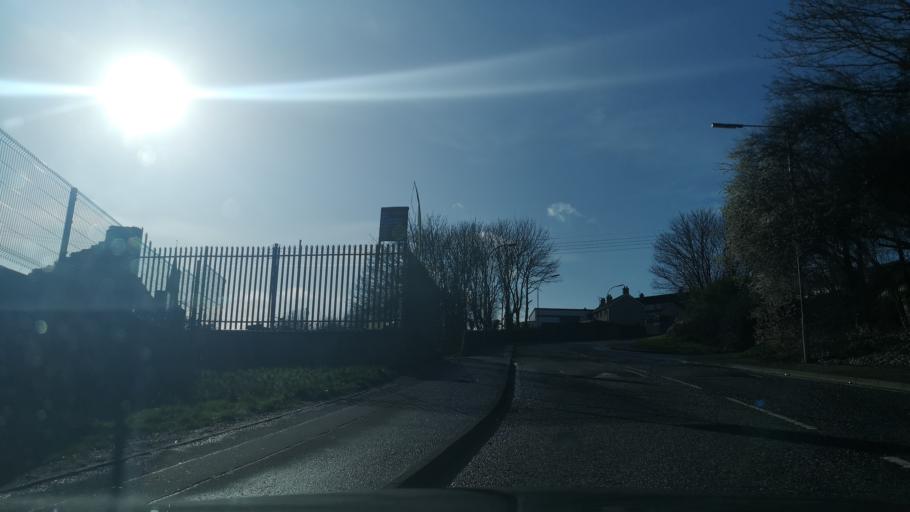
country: GB
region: Northern Ireland
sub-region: Newry and Mourne District
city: Newry
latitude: 54.1742
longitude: -6.3457
